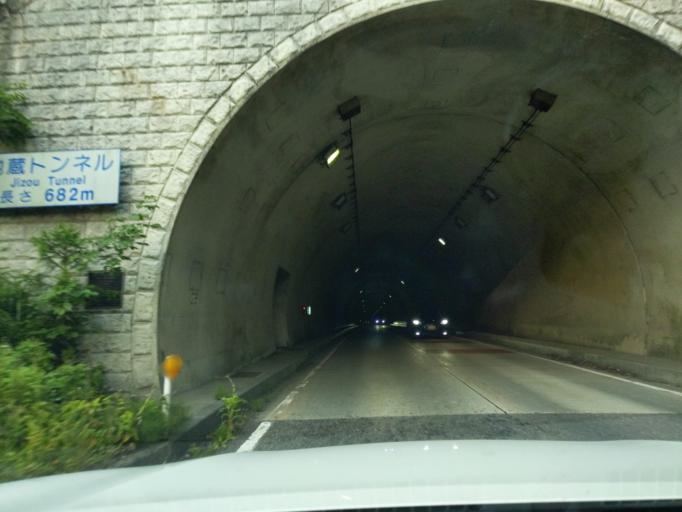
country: JP
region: Niigata
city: Nagaoka
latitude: 37.4458
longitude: 138.6911
